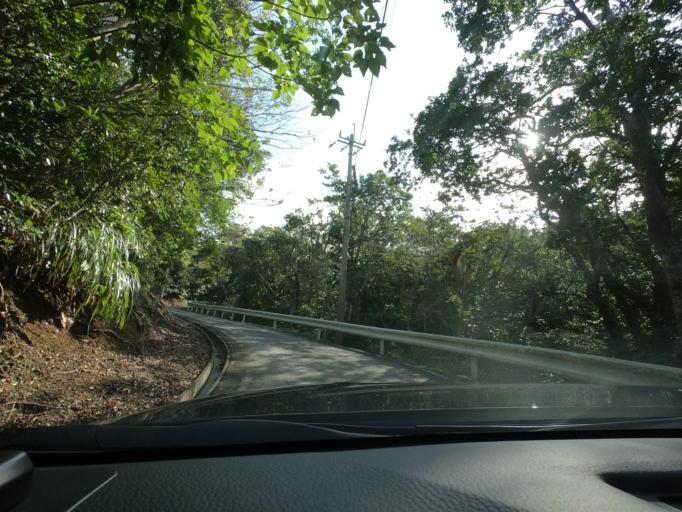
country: JP
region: Okinawa
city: Nago
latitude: 26.7561
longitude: 128.1990
